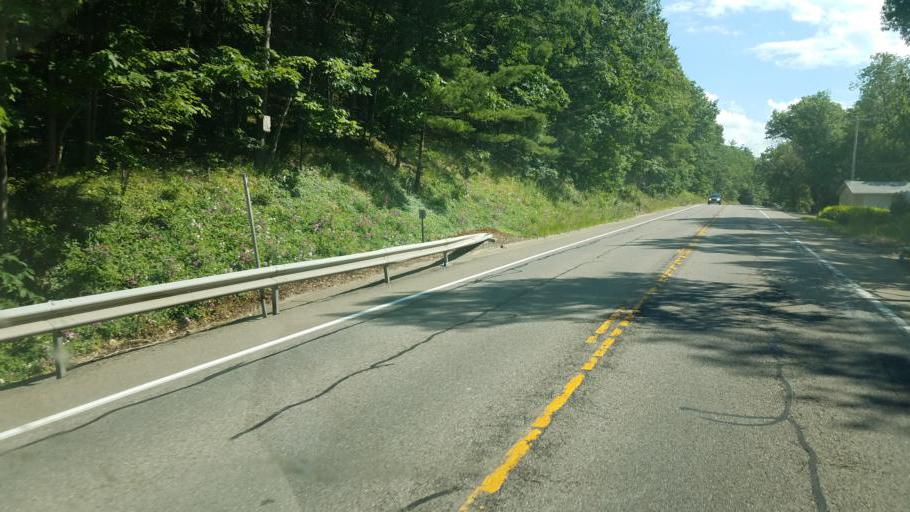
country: US
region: New York
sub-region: Steuben County
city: Sylvan Beach
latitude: 42.4500
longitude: -77.1666
